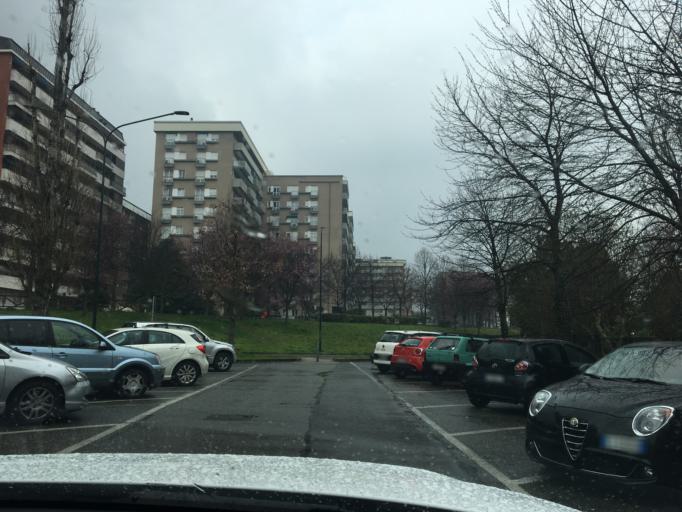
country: IT
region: Piedmont
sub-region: Provincia di Torino
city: Moncalieri
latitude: 45.0278
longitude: 7.6708
